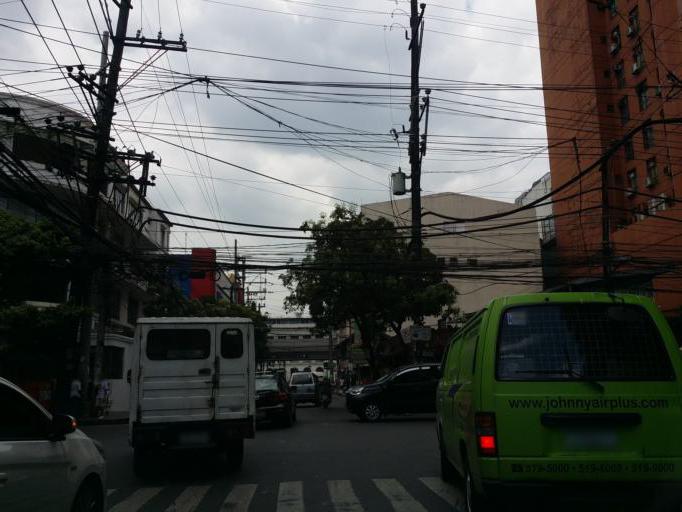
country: PH
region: Metro Manila
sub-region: City of Manila
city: Port Area
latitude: 14.5648
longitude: 120.9953
